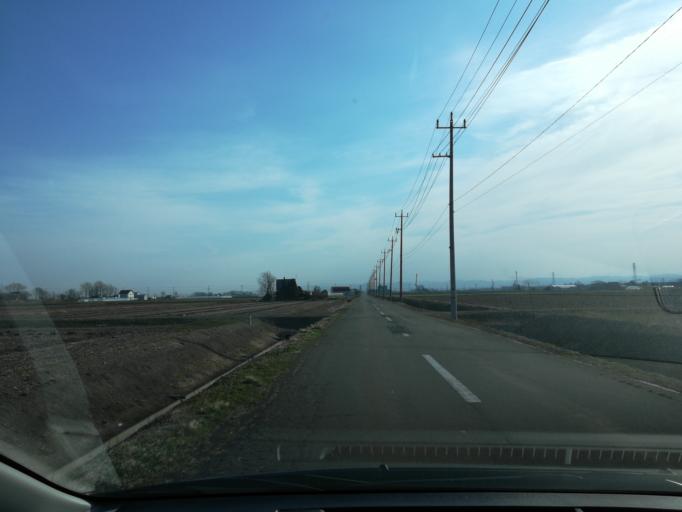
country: JP
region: Hokkaido
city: Ebetsu
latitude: 43.1571
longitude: 141.6419
